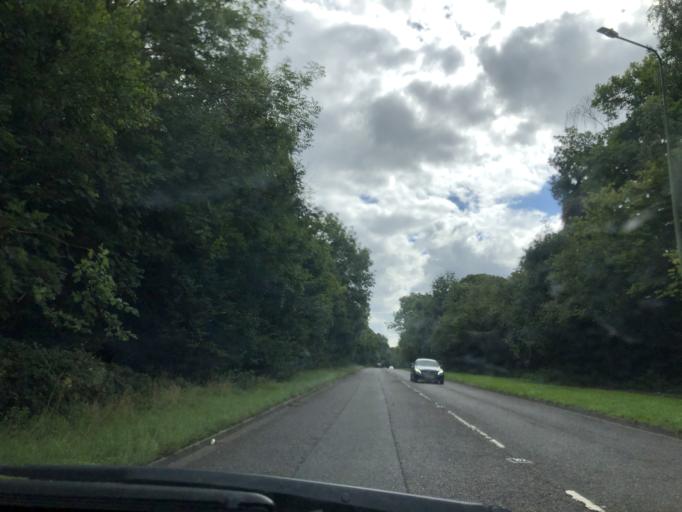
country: GB
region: England
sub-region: Kent
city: Halstead
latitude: 51.3440
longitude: 0.1403
